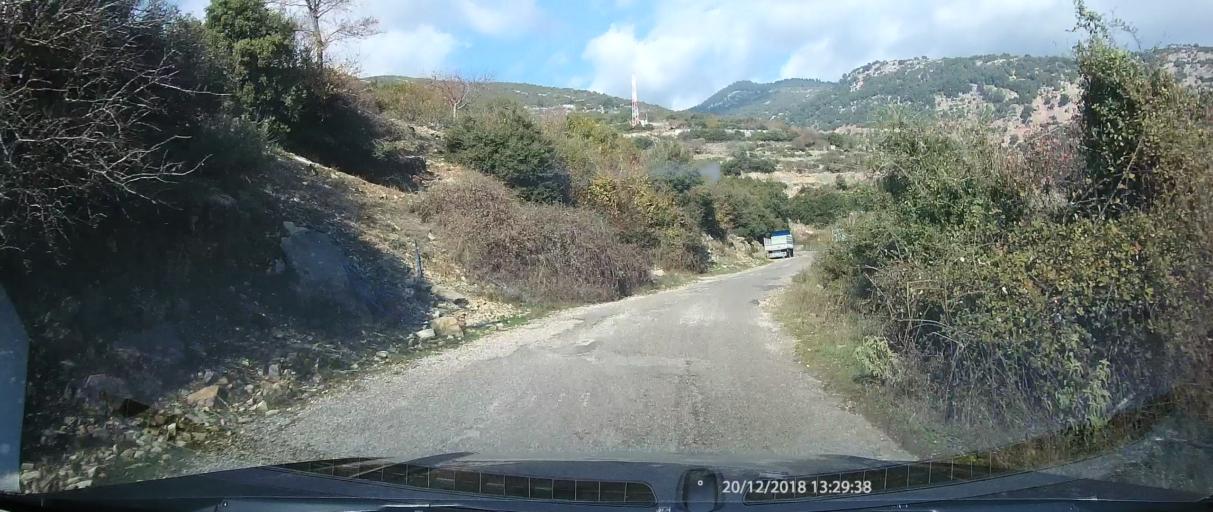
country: GR
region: West Greece
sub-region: Nomos Aitolias kai Akarnanias
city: Paravola
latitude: 38.6301
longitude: 21.5801
